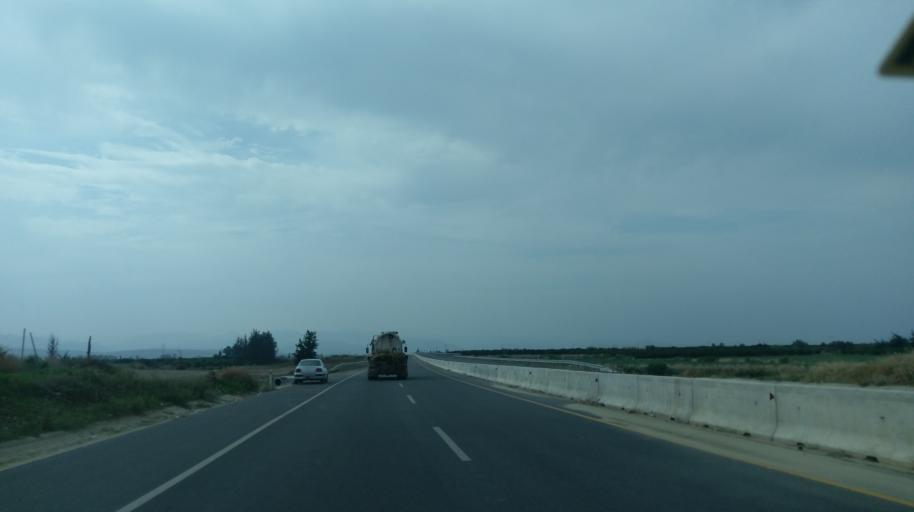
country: CY
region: Lefkosia
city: Morfou
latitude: 35.1619
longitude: 32.9286
